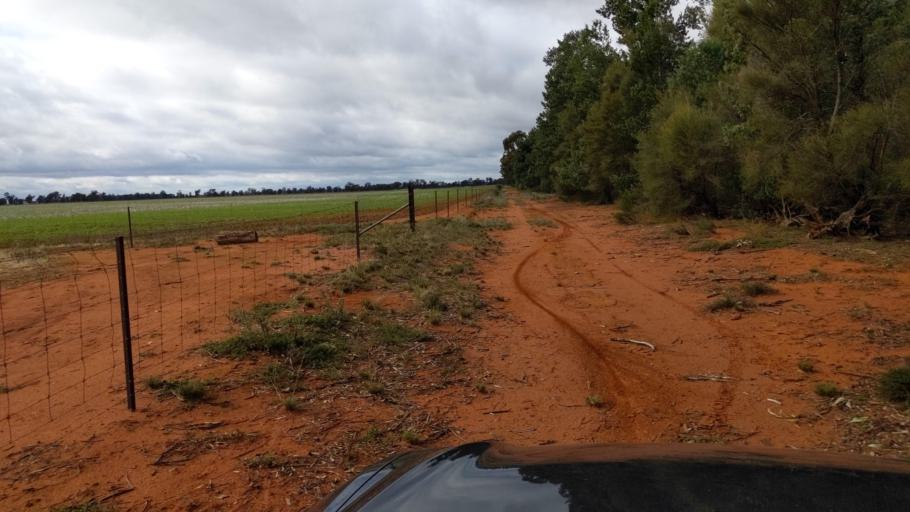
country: AU
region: New South Wales
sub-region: Coolamon
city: Coolamon
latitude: -34.8262
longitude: 146.9336
